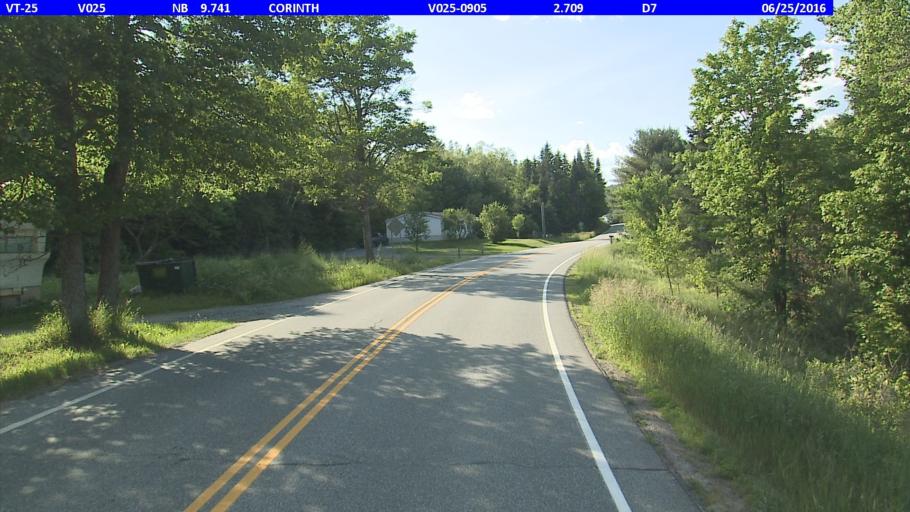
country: US
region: New Hampshire
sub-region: Grafton County
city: Haverhill
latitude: 44.0657
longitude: -72.2433
